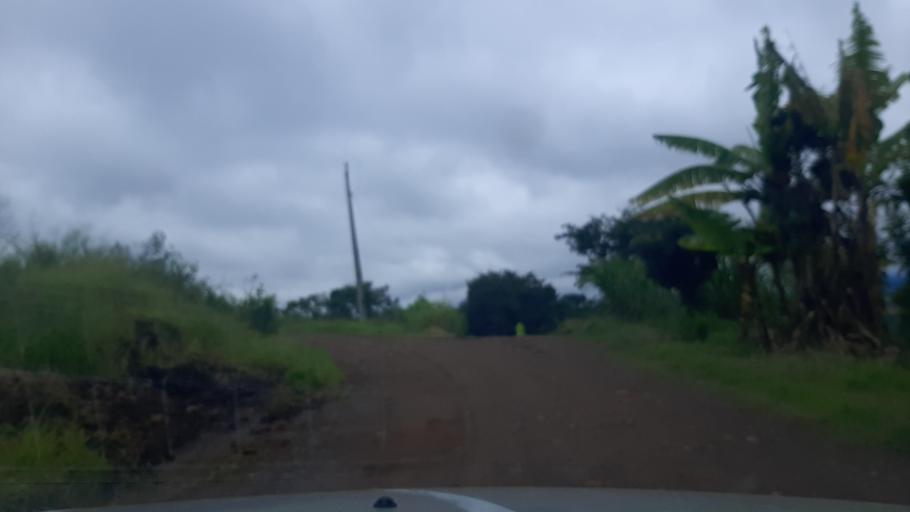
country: BR
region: Parana
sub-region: Ampere
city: Ampere
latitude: -26.0569
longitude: -53.5529
